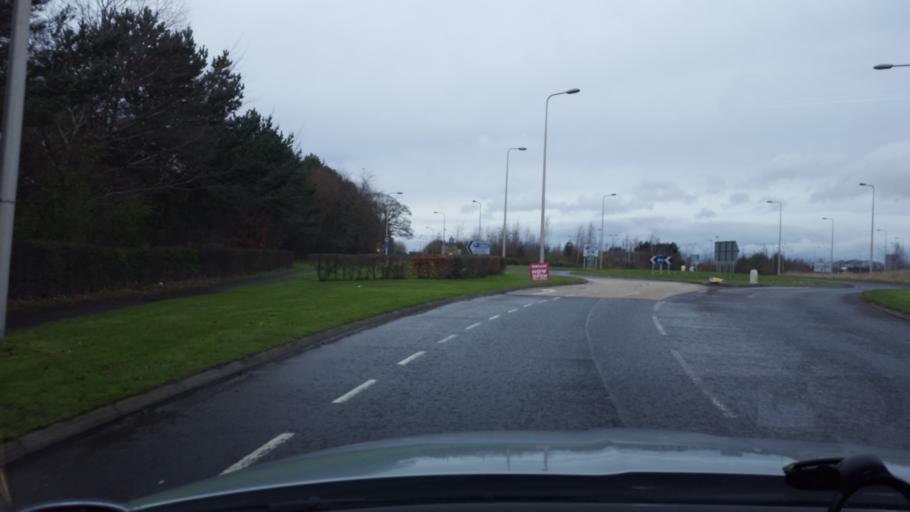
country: GB
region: Scotland
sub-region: Edinburgh
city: Currie
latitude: 55.9147
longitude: -3.3139
